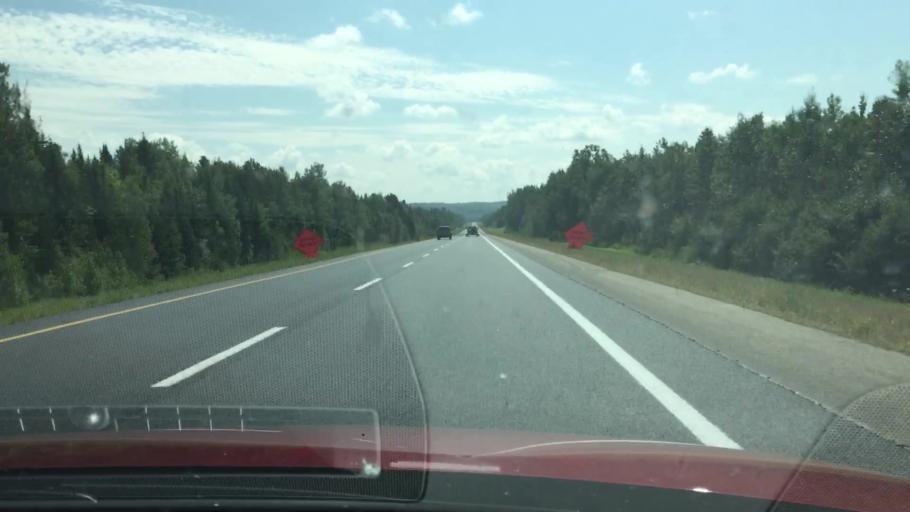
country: US
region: Maine
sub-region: Penobscot County
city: Patten
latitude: 45.8253
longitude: -68.4321
